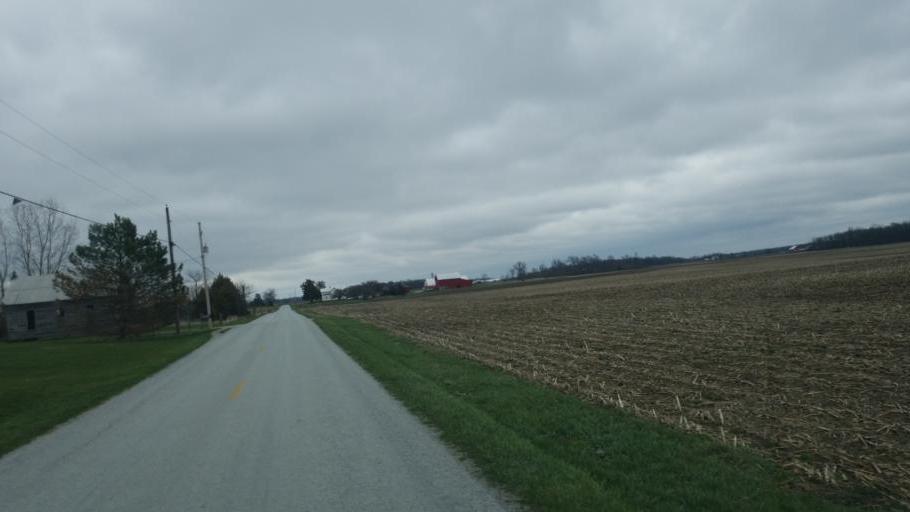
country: US
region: Ohio
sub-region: Hardin County
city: Kenton
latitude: 40.6575
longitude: -83.4934
